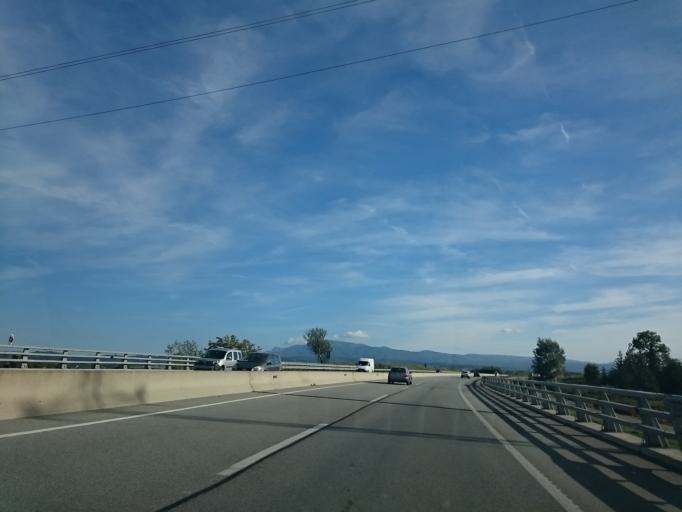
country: ES
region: Catalonia
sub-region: Provincia de Barcelona
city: Vic
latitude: 41.9233
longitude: 2.2349
